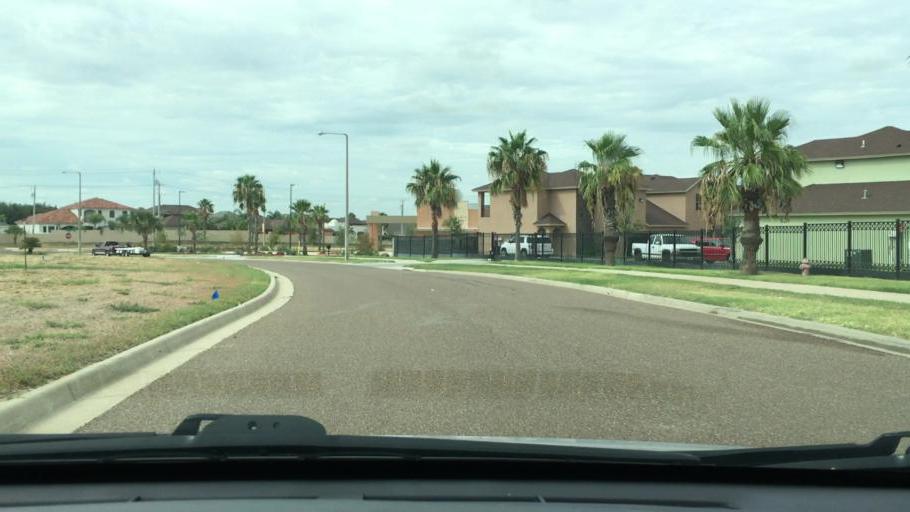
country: US
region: Texas
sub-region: Webb County
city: Laredo
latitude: 27.6045
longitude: -99.4831
